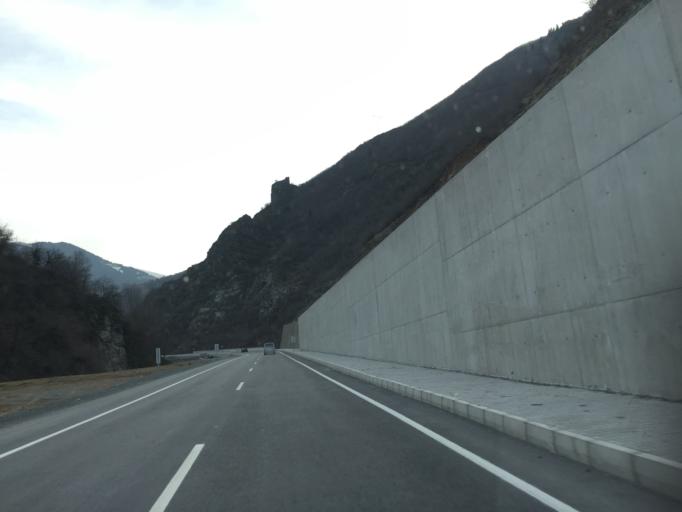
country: TR
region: Trabzon
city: Macka
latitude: 40.7736
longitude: 39.5669
